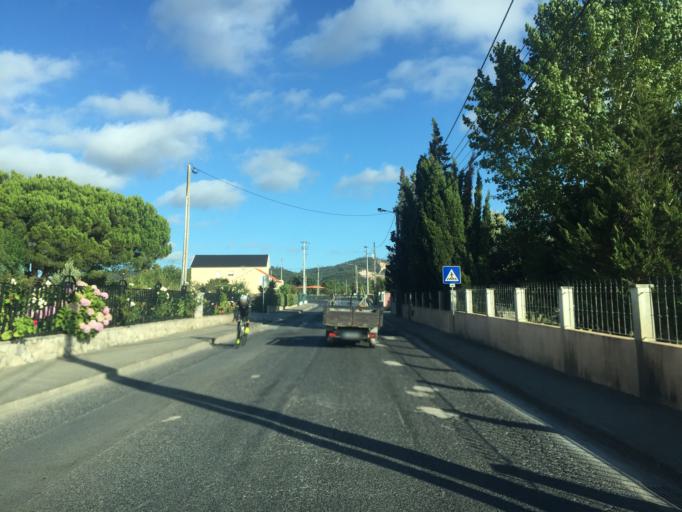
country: PT
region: Lisbon
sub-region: Torres Vedras
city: A dos Cunhados
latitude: 39.1466
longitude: -9.2843
